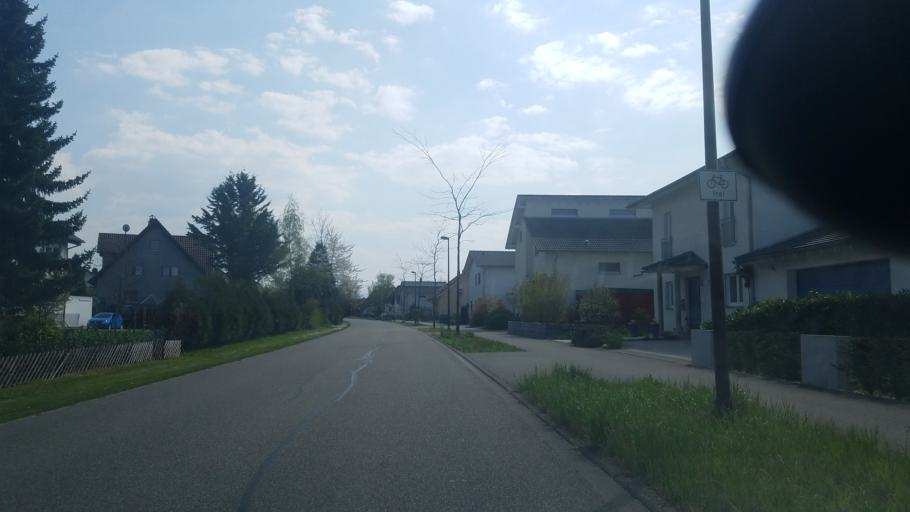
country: DE
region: Baden-Wuerttemberg
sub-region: Freiburg Region
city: Achern
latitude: 48.6307
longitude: 8.0447
